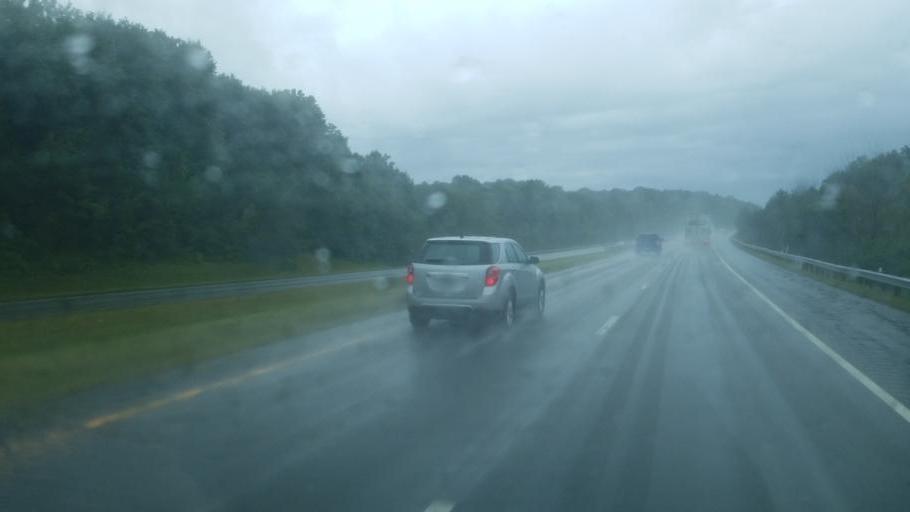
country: US
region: Ohio
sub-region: Summit County
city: Montrose-Ghent
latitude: 41.1975
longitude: -81.6961
